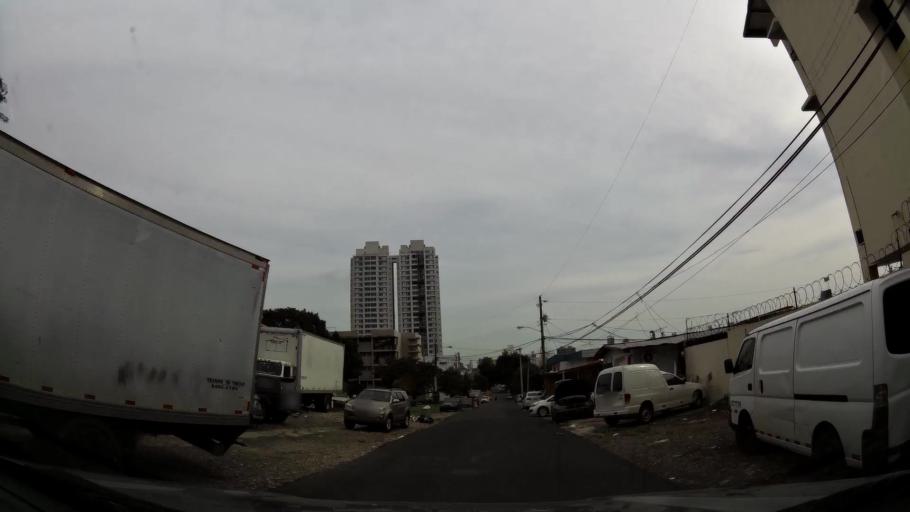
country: PA
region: Panama
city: Panama
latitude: 9.0109
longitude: -79.5205
